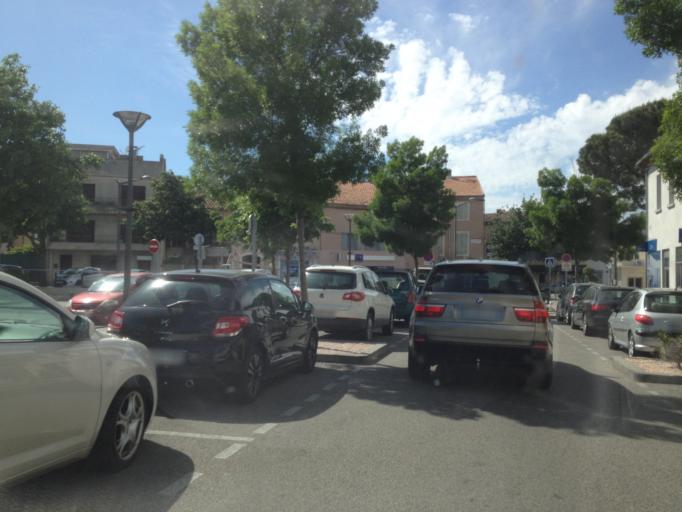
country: FR
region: Provence-Alpes-Cote d'Azur
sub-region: Departement du Vaucluse
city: Sorgues
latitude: 44.0083
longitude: 4.8733
